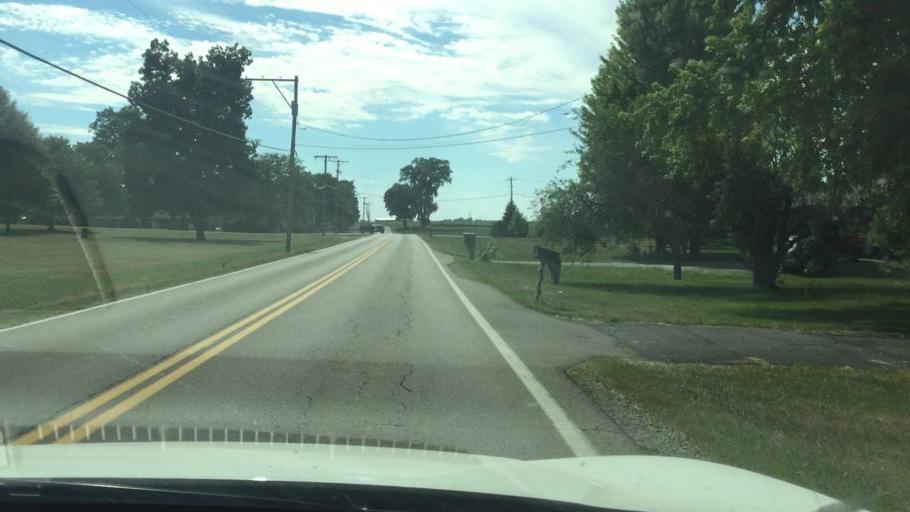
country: US
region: Ohio
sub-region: Clark County
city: Lisbon
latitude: 39.9419
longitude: -83.6801
